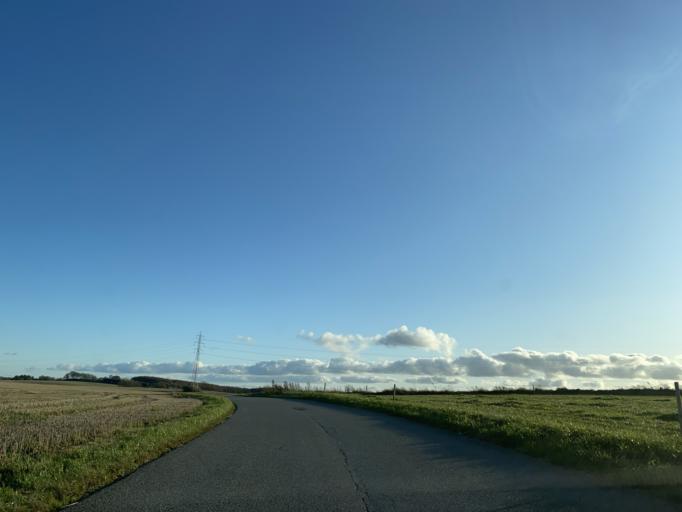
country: DK
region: Central Jutland
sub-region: Viborg Kommune
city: Bjerringbro
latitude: 56.3513
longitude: 9.7172
